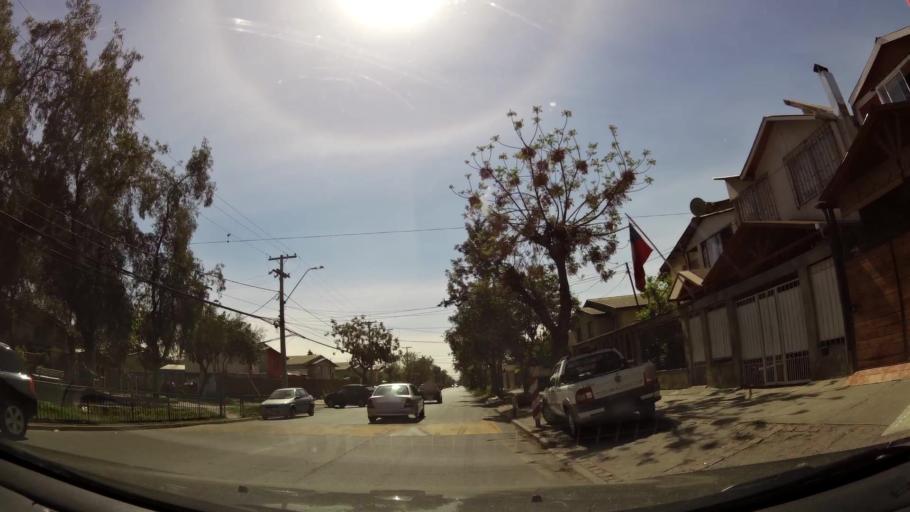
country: CL
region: Santiago Metropolitan
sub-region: Provincia de Cordillera
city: Puente Alto
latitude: -33.5710
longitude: -70.5614
